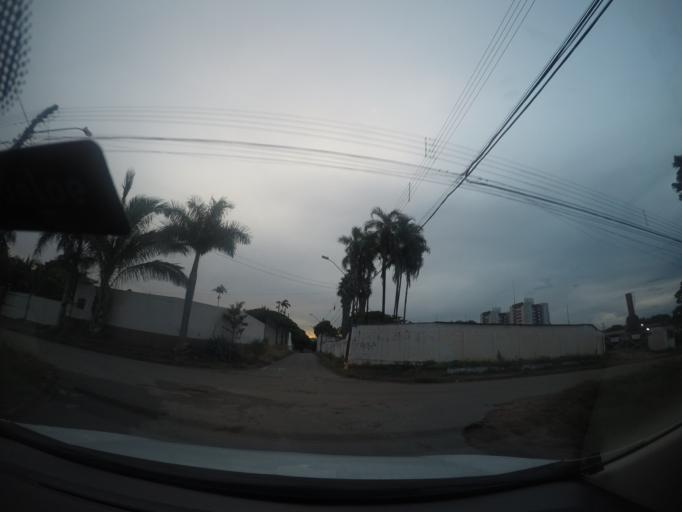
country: BR
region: Goias
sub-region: Goiania
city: Goiania
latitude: -16.6440
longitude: -49.2433
